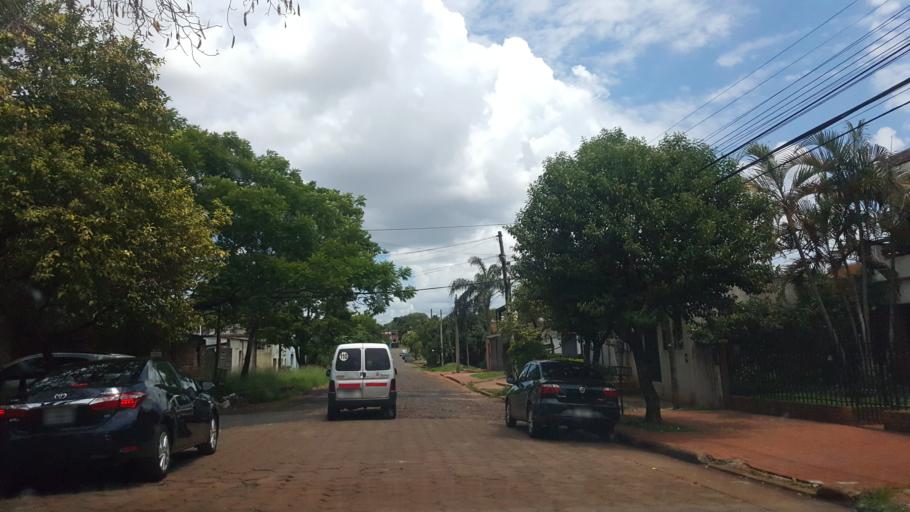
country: AR
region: Misiones
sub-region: Departamento de Capital
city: Posadas
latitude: -27.3808
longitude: -55.9089
